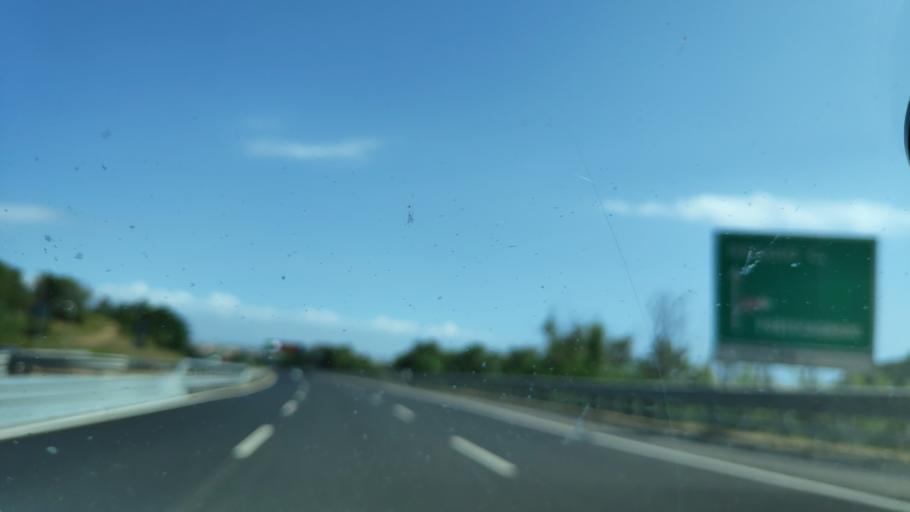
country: IT
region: Campania
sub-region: Provincia di Salerno
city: Fuorni
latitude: 40.6623
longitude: 14.8592
